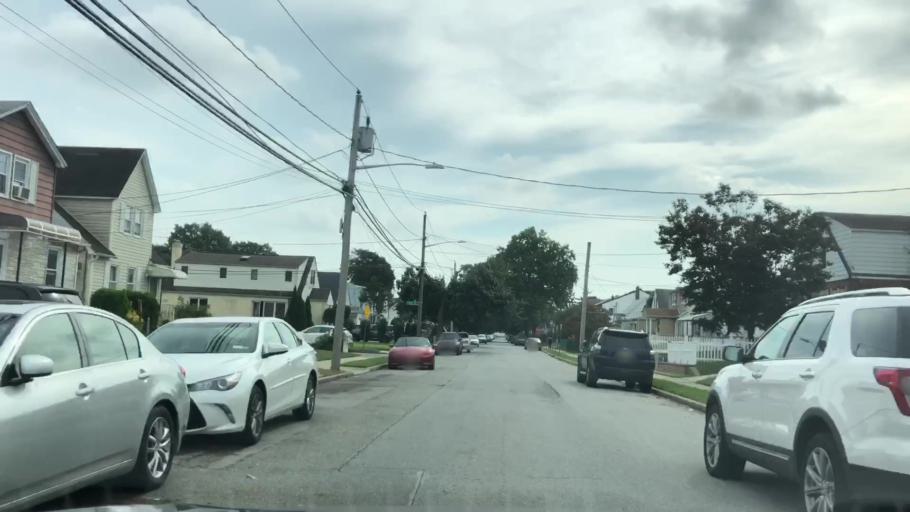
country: US
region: New York
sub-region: Nassau County
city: South Floral Park
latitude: 40.7060
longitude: -73.6923
